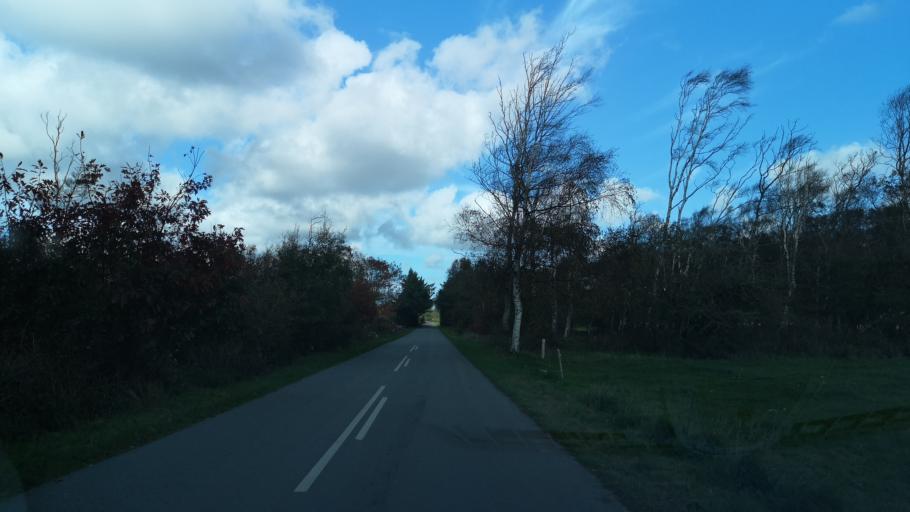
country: DK
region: South Denmark
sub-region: Varde Kommune
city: Oksbol
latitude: 55.7036
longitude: 8.2759
